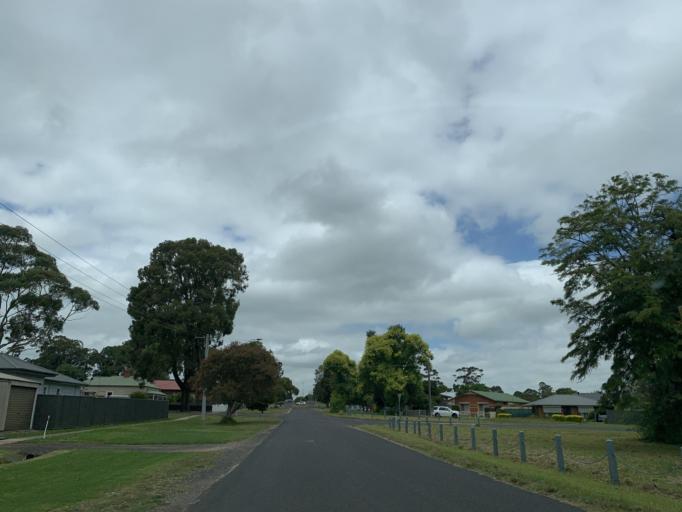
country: AU
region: Victoria
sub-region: Wellington
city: Sale
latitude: -37.9611
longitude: 146.9776
